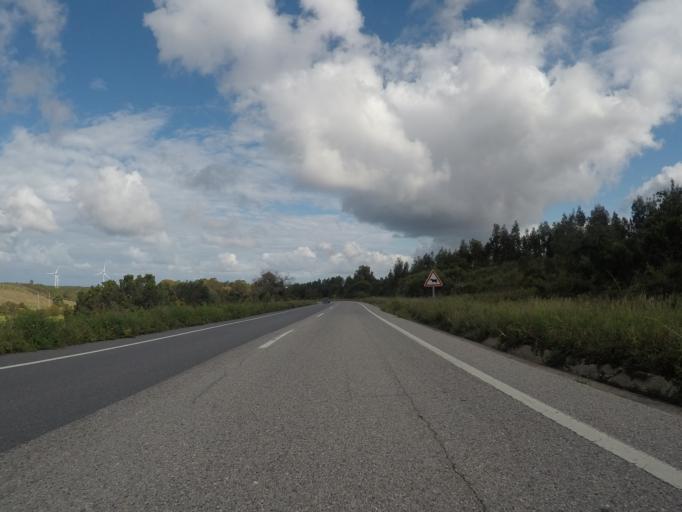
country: PT
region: Faro
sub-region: Aljezur
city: Aljezur
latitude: 37.2223
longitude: -8.7816
